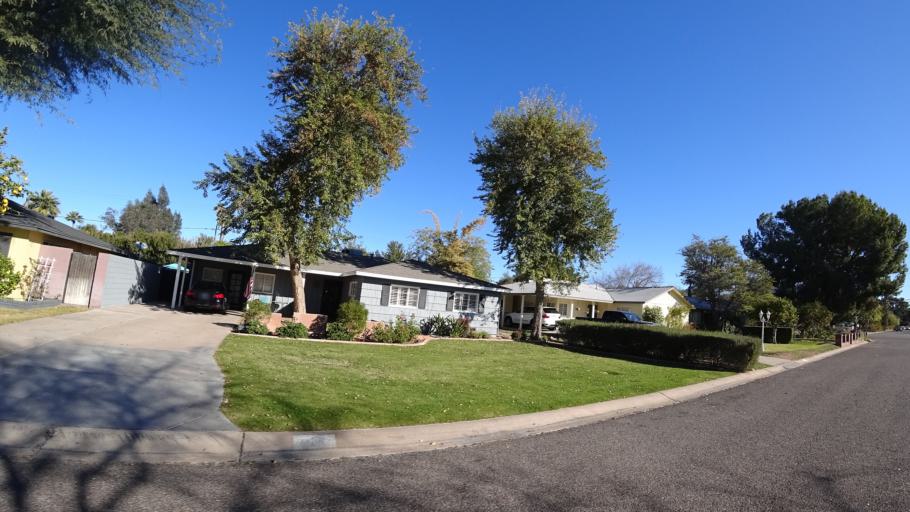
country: US
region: Arizona
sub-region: Maricopa County
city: Paradise Valley
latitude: 33.5049
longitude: -112.0050
